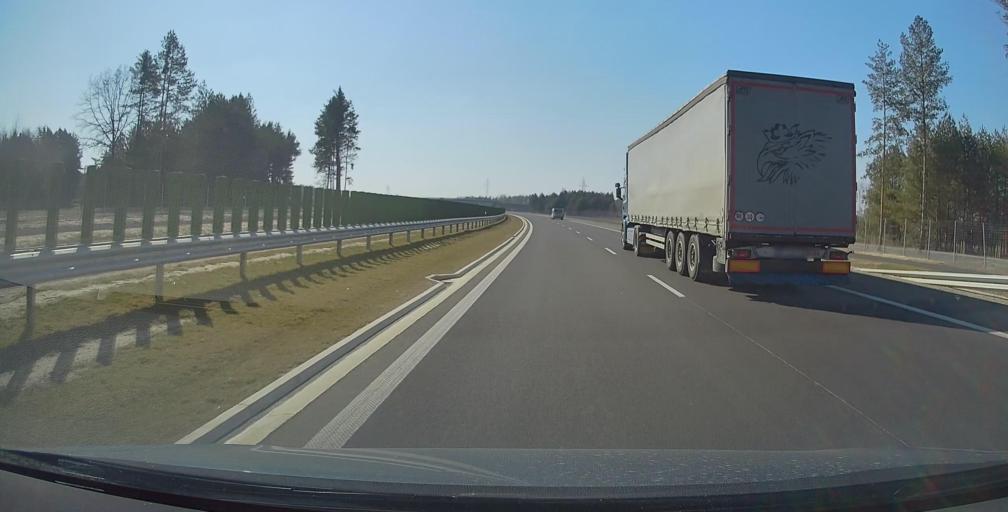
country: PL
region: Subcarpathian Voivodeship
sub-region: Powiat nizanski
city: Konczyce
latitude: 50.4281
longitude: 22.1306
